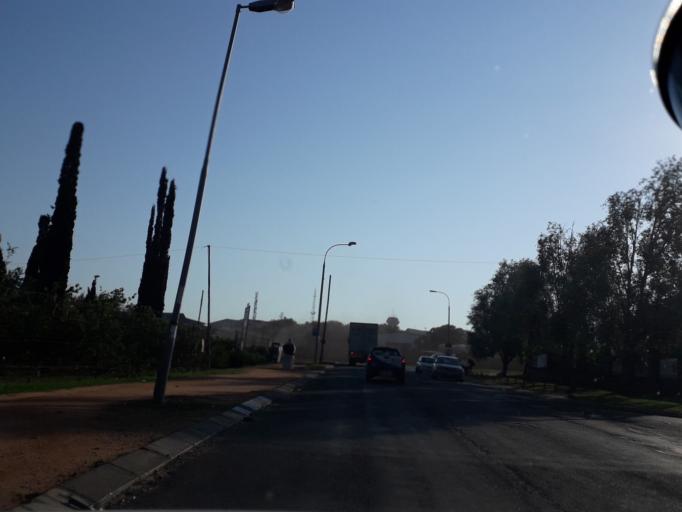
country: ZA
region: Gauteng
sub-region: West Rand District Municipality
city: Muldersdriseloop
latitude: -26.0794
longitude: 27.9208
